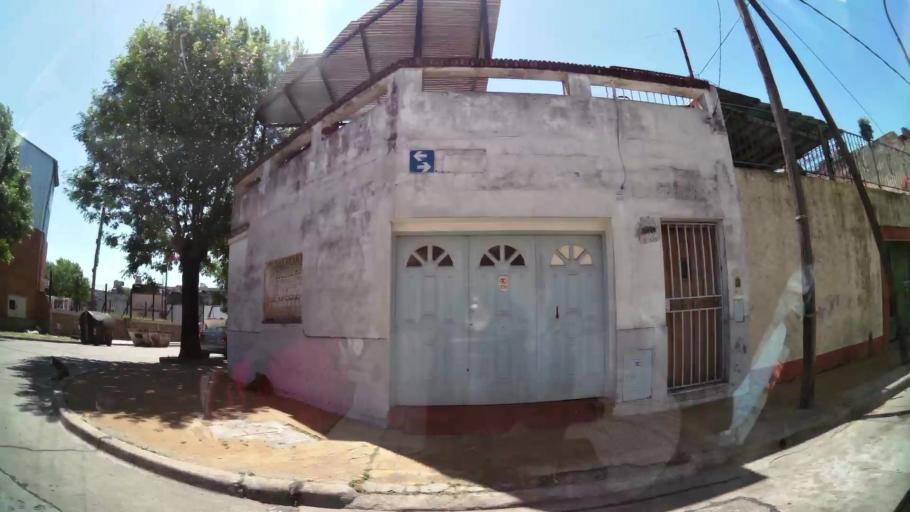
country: AR
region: Buenos Aires
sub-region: Partido de Avellaneda
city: Avellaneda
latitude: -34.6577
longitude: -58.4113
